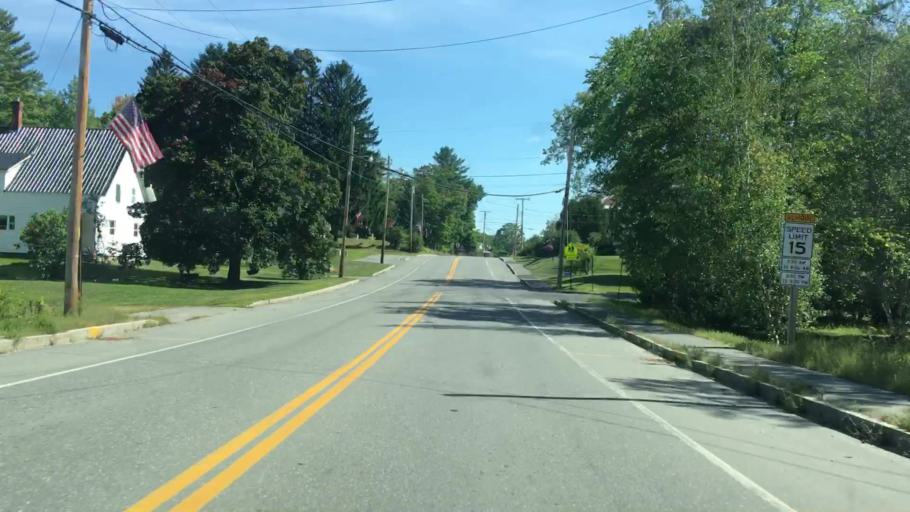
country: US
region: Maine
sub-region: Piscataquis County
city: Milo
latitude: 45.2512
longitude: -68.9837
